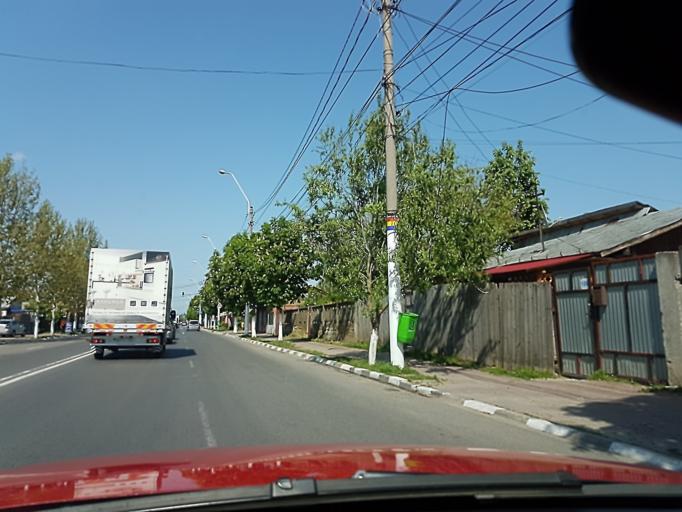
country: RO
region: Ilfov
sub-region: Voluntari City
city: Voluntari
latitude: 44.4923
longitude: 26.1720
